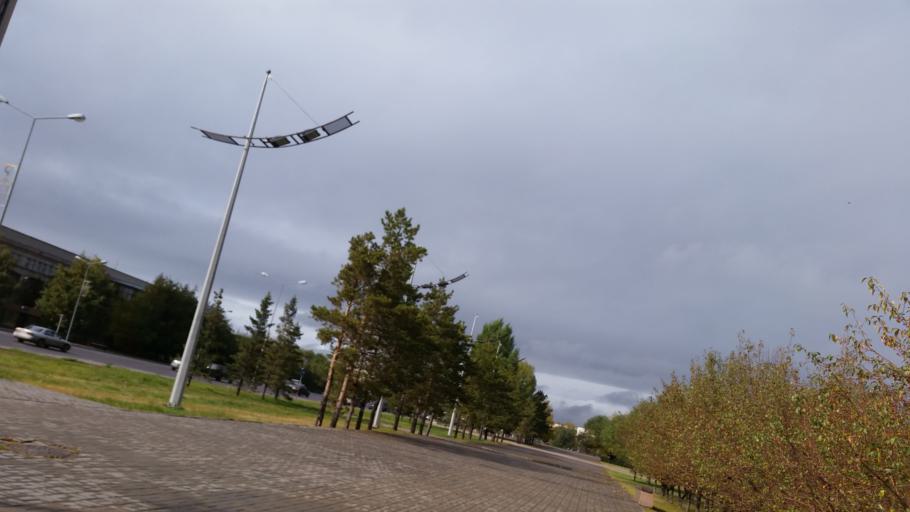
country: KZ
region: Astana Qalasy
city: Astana
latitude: 51.1520
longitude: 71.4565
